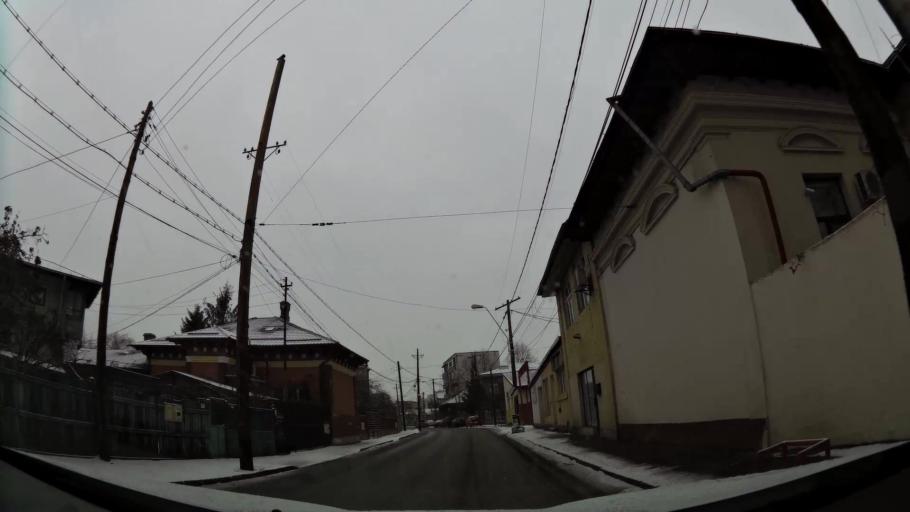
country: RO
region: Prahova
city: Ploiesti
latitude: 44.9373
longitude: 26.0171
